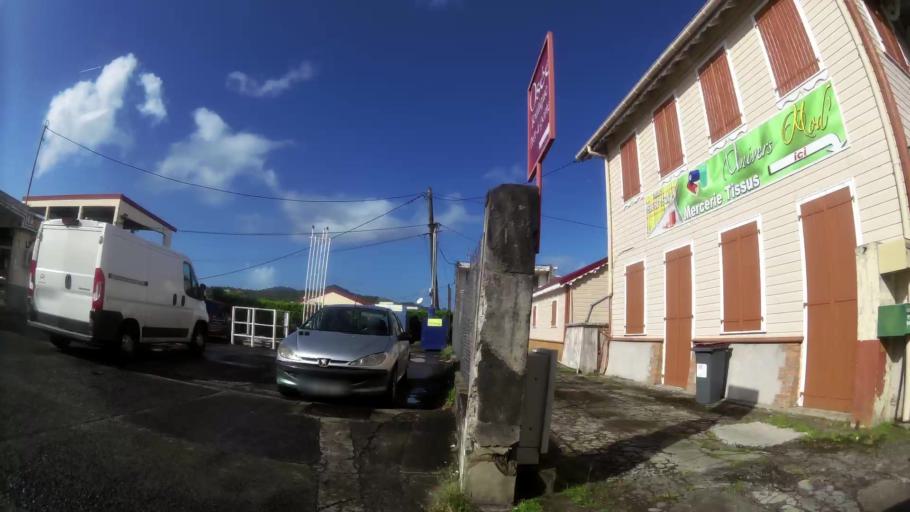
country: MQ
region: Martinique
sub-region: Martinique
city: Ducos
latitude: 14.5281
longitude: -60.9808
